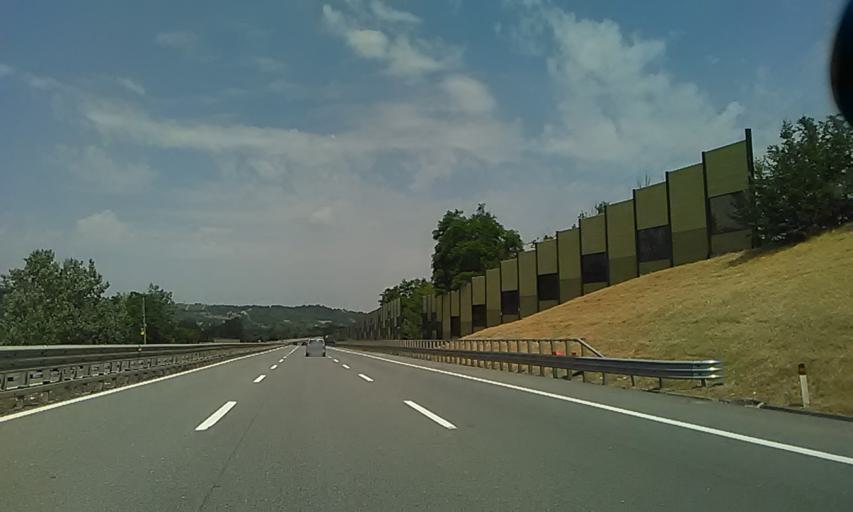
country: IT
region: Piedmont
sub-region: Provincia di Alessandria
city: Rocca Grimalda
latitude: 44.6569
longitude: 8.6594
